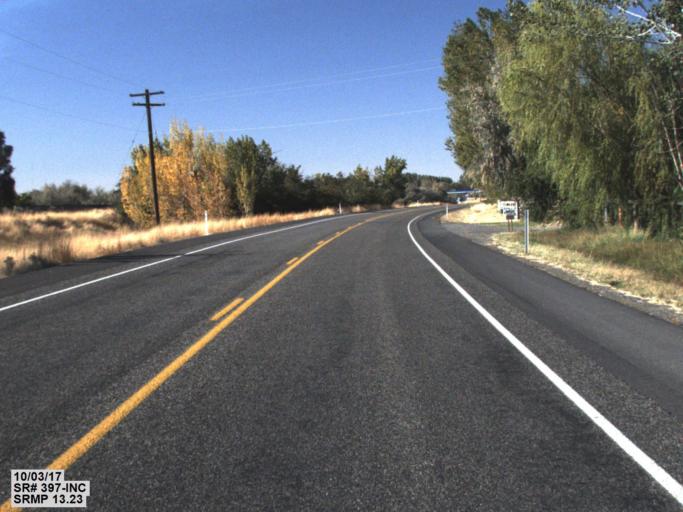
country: US
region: Washington
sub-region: Benton County
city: Finley
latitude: 46.1659
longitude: -119.0468
